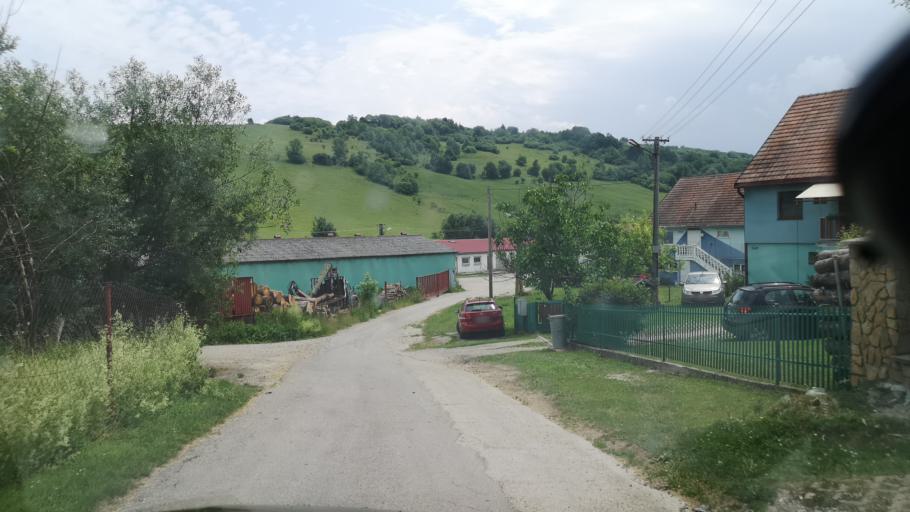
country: SK
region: Zilinsky
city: Ruzomberok
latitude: 49.1222
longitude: 19.4112
